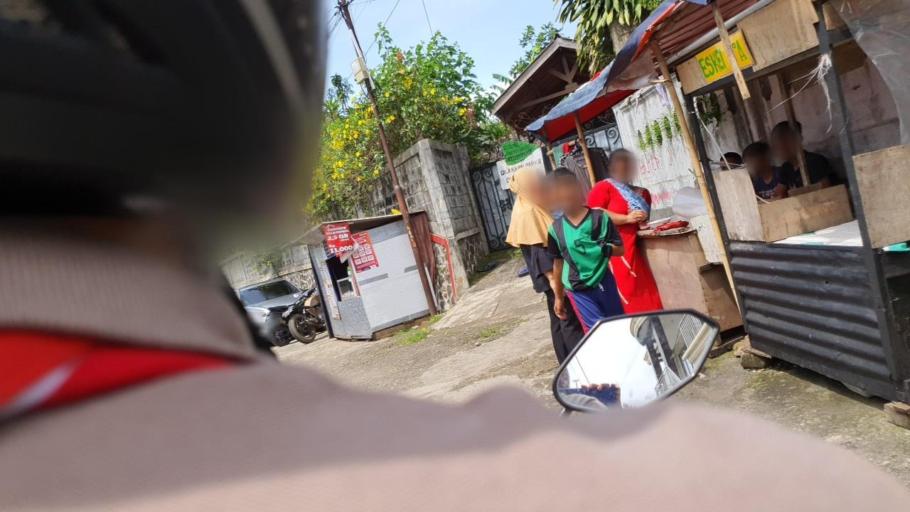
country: ID
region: West Java
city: Caringin
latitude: -6.6512
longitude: 106.9019
